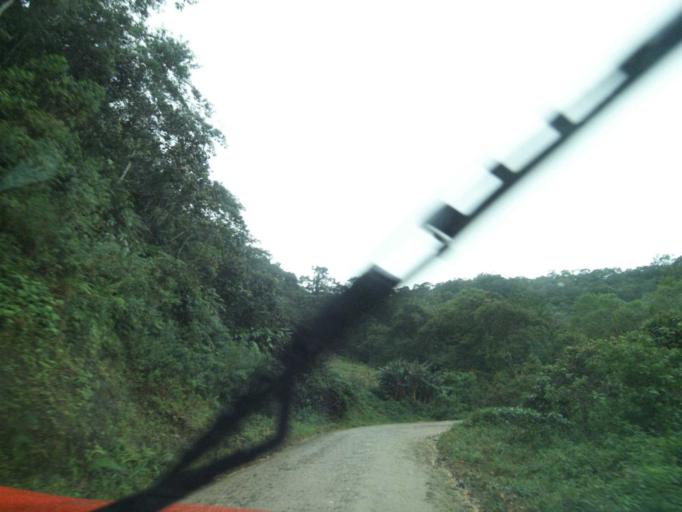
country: BR
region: Santa Catarina
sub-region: Anitapolis
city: Anitapolis
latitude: -27.9247
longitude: -49.1829
